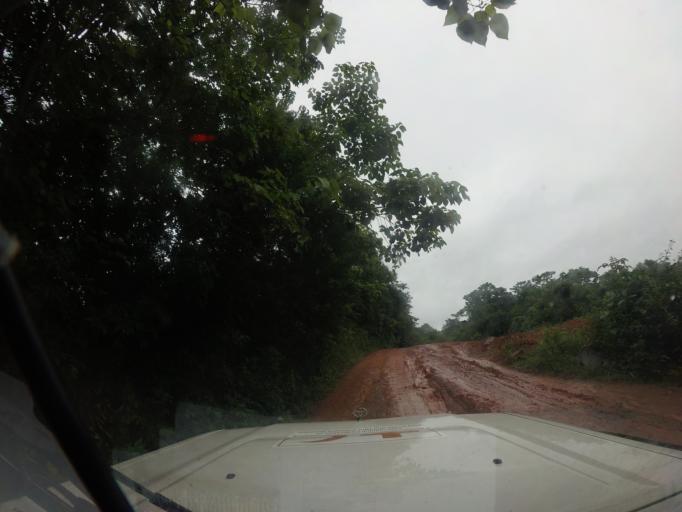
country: SL
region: Northern Province
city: Kabala
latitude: 9.6315
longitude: -11.5492
